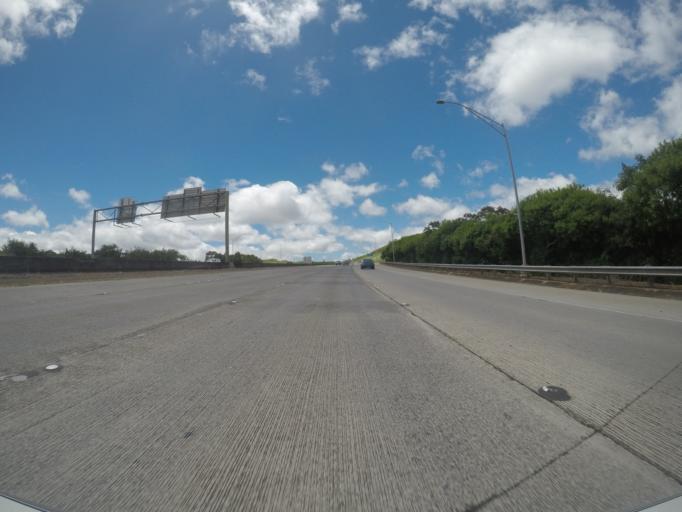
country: US
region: Hawaii
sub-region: Honolulu County
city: Waipio
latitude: 21.4082
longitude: -157.9894
